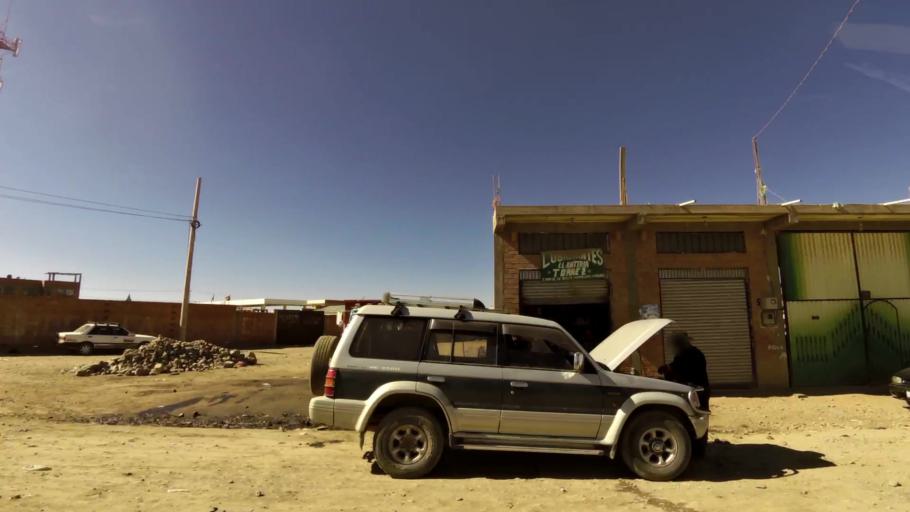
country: BO
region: La Paz
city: La Paz
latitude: -16.6199
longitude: -68.1839
